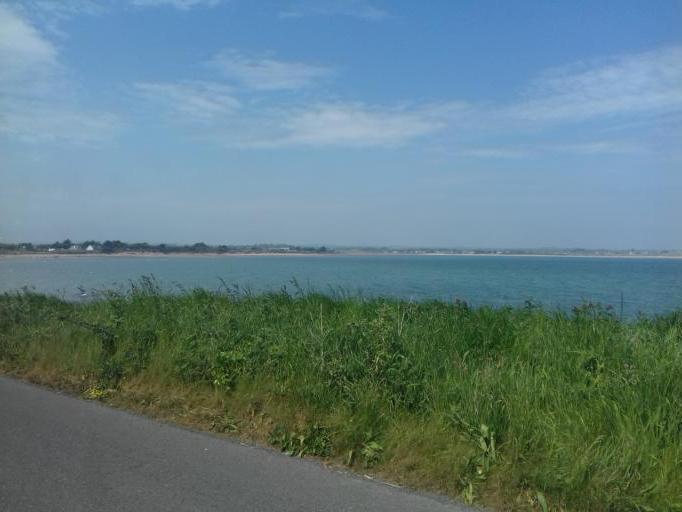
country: IE
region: Leinster
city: Portraine
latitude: 53.4928
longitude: -6.1026
